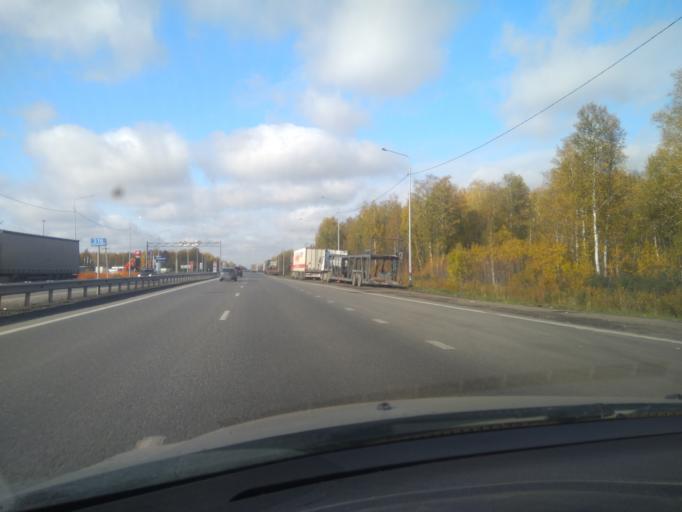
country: RU
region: Tjumen
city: Moskovskiy
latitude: 57.1134
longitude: 65.4061
